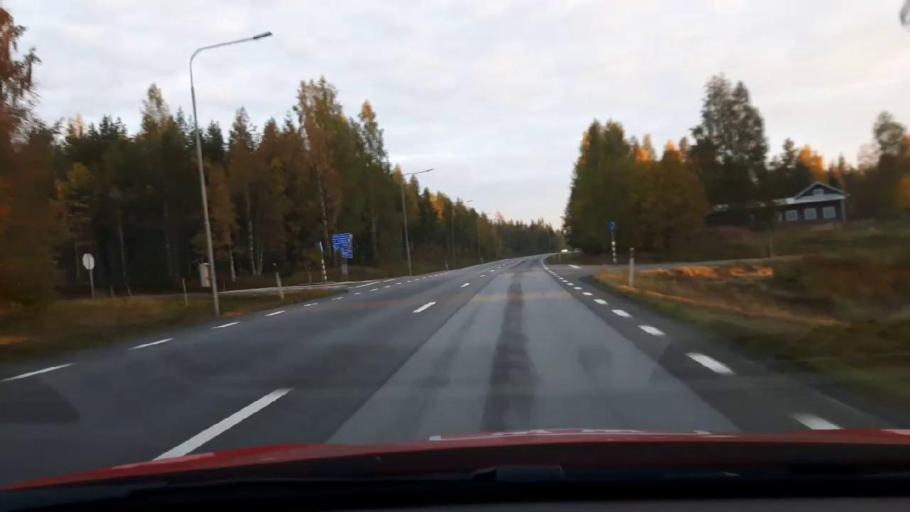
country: SE
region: Jaemtland
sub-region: OEstersunds Kommun
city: Lit
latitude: 63.3086
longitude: 14.8706
